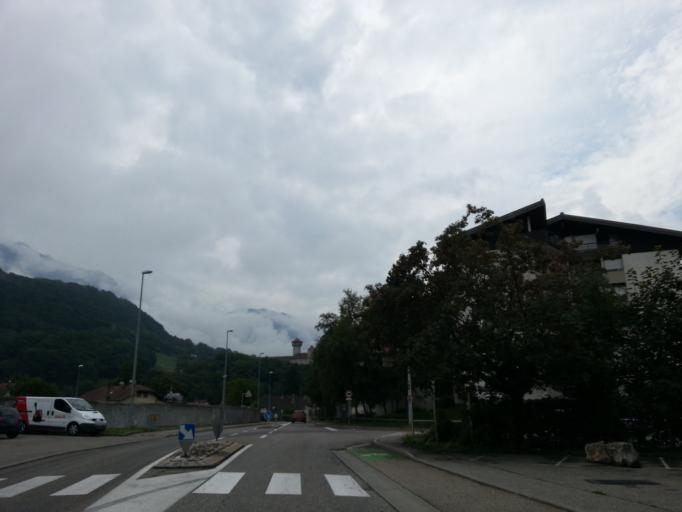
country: FR
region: Rhone-Alpes
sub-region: Departement de la Haute-Savoie
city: Faverges
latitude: 45.7502
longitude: 6.2946
